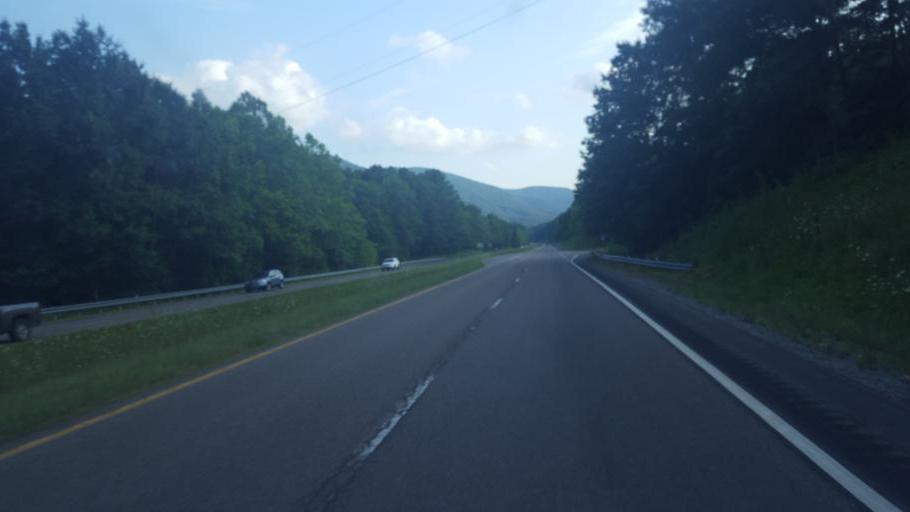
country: US
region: Virginia
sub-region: Wise County
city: Big Stone Gap
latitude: 36.8473
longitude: -82.7605
